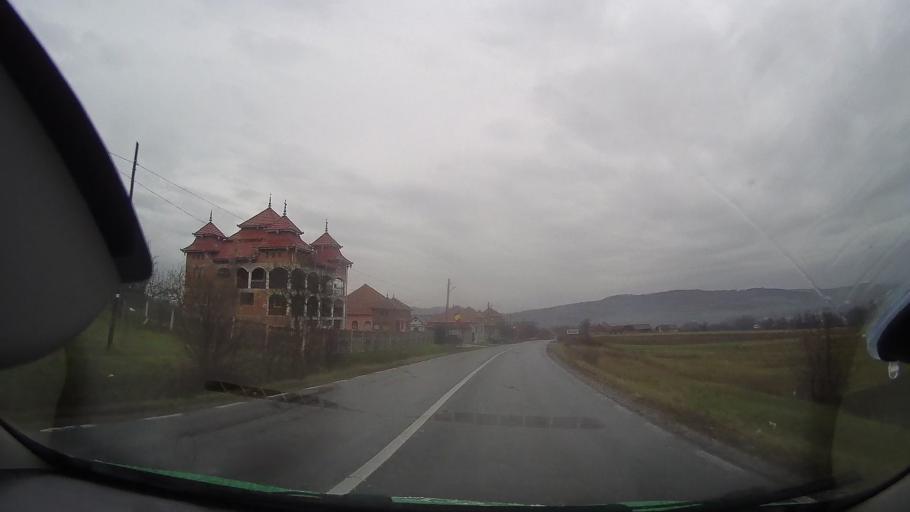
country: RO
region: Bihor
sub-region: Comuna Rabagani
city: Rabagani
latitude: 46.7432
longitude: 22.2277
